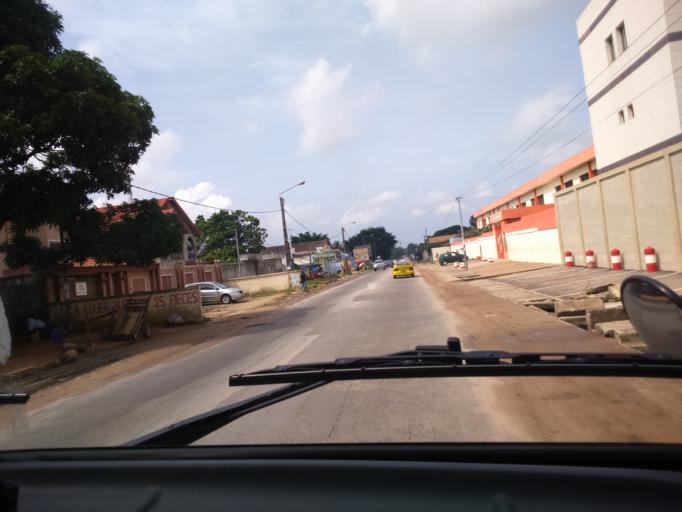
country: CI
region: Lagunes
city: Abobo
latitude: 5.3647
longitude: -3.9793
